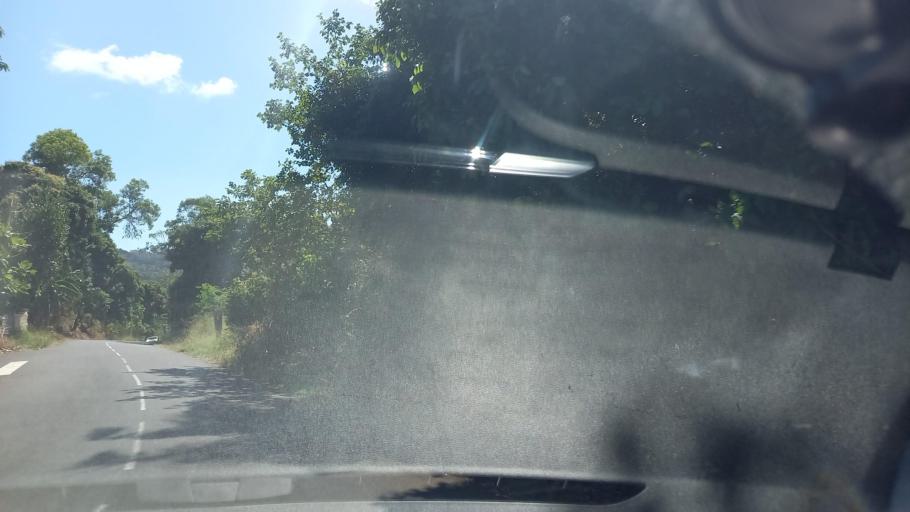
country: YT
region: Kani-Keli
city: Kani Keli
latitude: -12.9635
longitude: 45.1134
